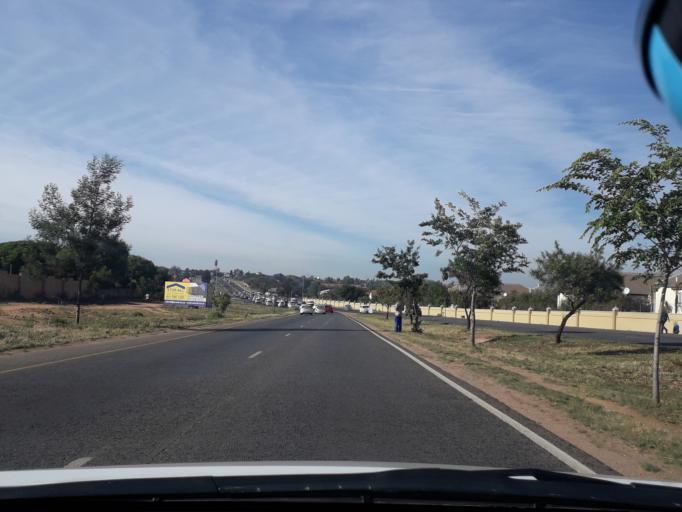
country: ZA
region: Gauteng
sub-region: City of Johannesburg Metropolitan Municipality
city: Roodepoort
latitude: -26.0919
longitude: 27.9273
